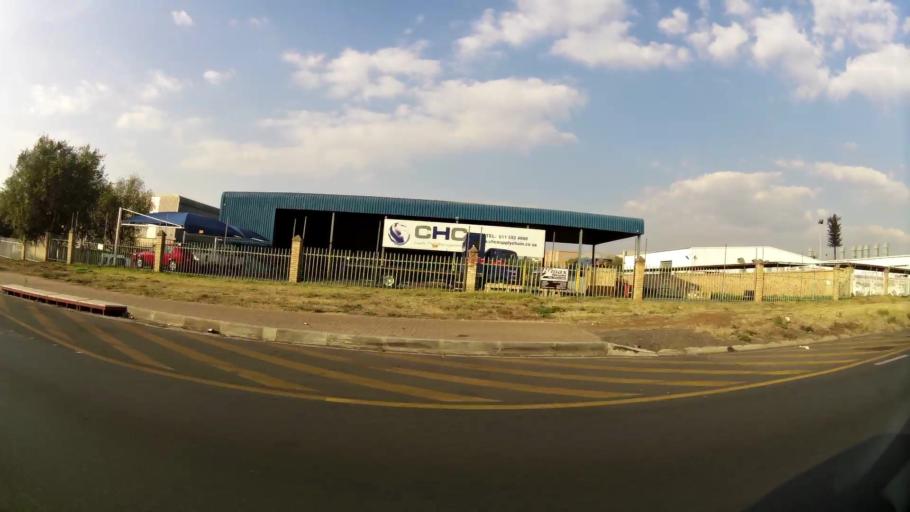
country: ZA
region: Gauteng
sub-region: City of Johannesburg Metropolitan Municipality
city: Modderfontein
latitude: -26.1170
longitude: 28.1995
